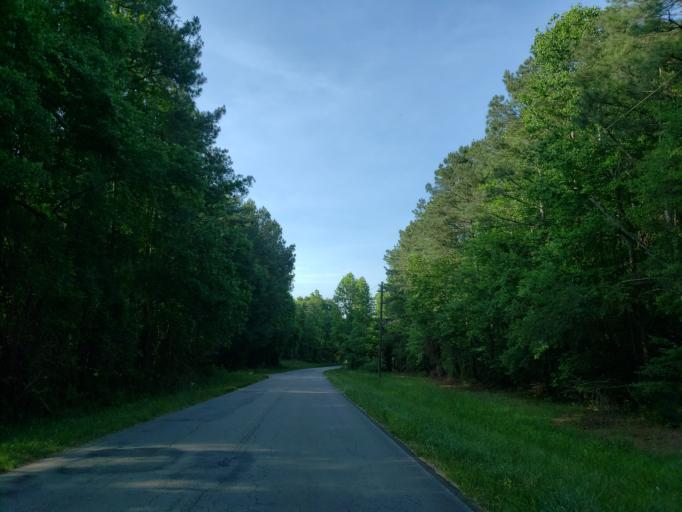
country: US
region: Georgia
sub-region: Carroll County
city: Bowdon
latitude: 33.4772
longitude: -85.3030
